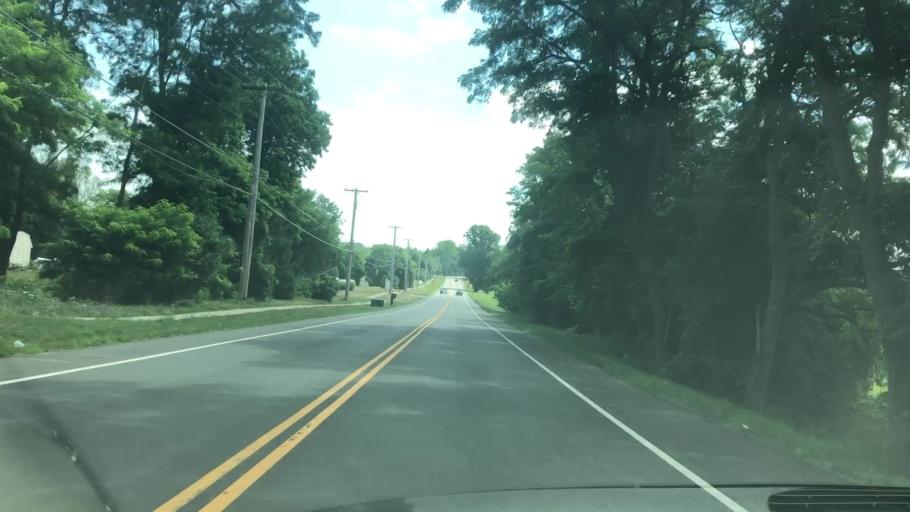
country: US
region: New York
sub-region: Monroe County
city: Fairport
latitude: 43.0794
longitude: -77.3987
